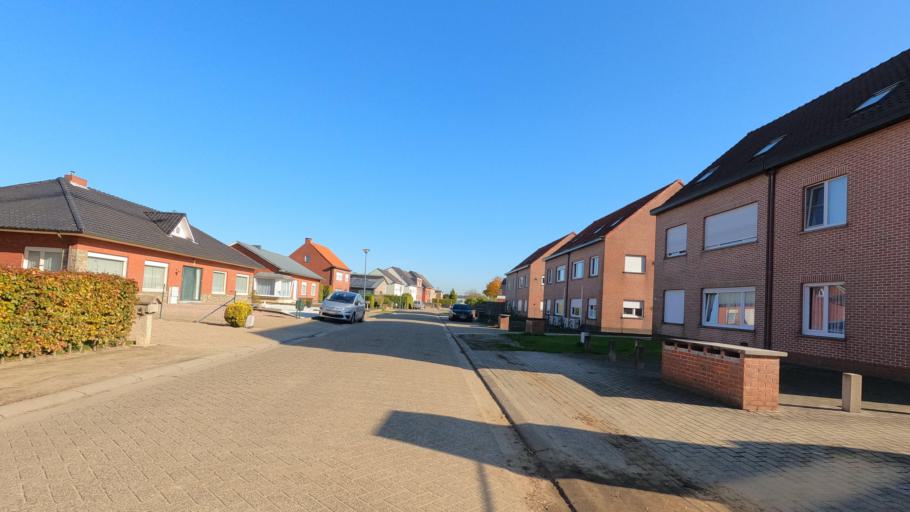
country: BE
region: Flanders
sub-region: Provincie Antwerpen
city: Oostmalle
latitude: 51.3013
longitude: 4.6998
